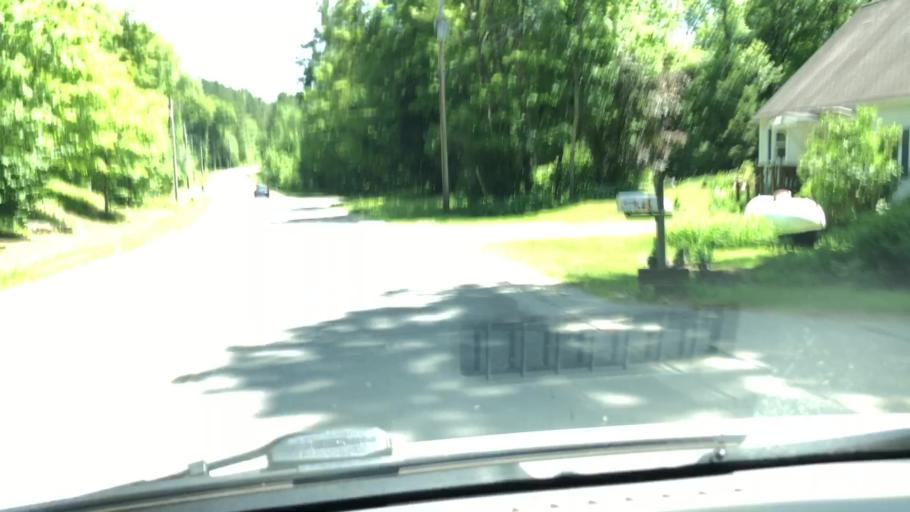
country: US
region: Massachusetts
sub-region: Franklin County
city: Charlemont
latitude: 42.5261
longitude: -72.9294
